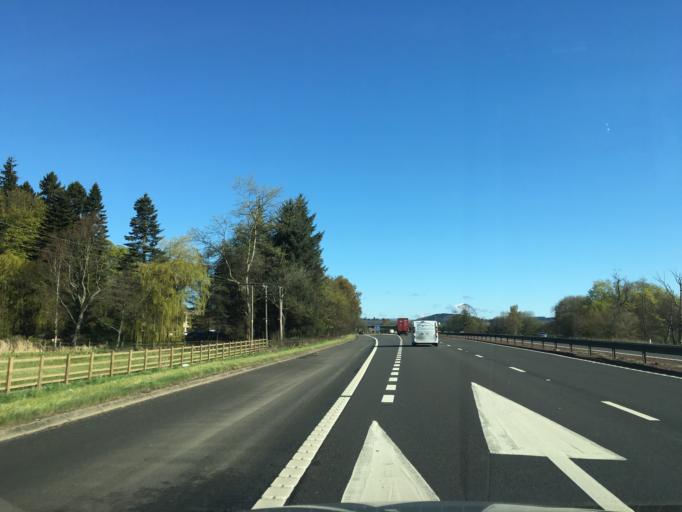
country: GB
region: Scotland
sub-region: Stirling
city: Bridge of Allan
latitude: 56.1292
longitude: -3.9709
